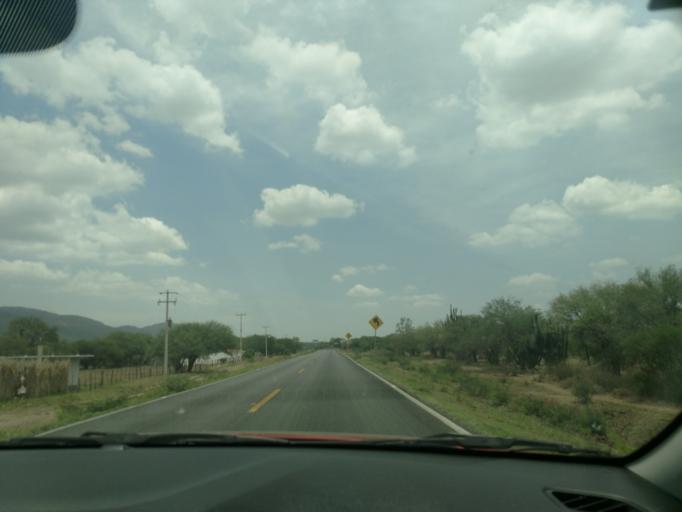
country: MX
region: San Luis Potosi
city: Villa Juarez
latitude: 22.0186
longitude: -100.3899
